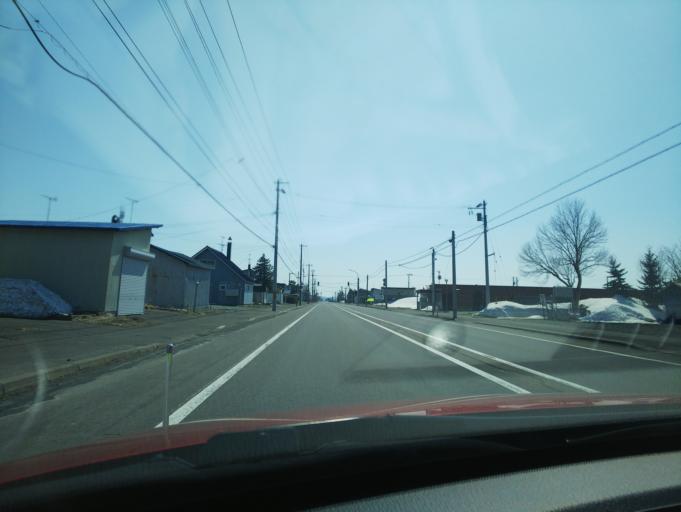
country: JP
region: Hokkaido
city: Nayoro
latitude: 44.2383
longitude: 142.3948
